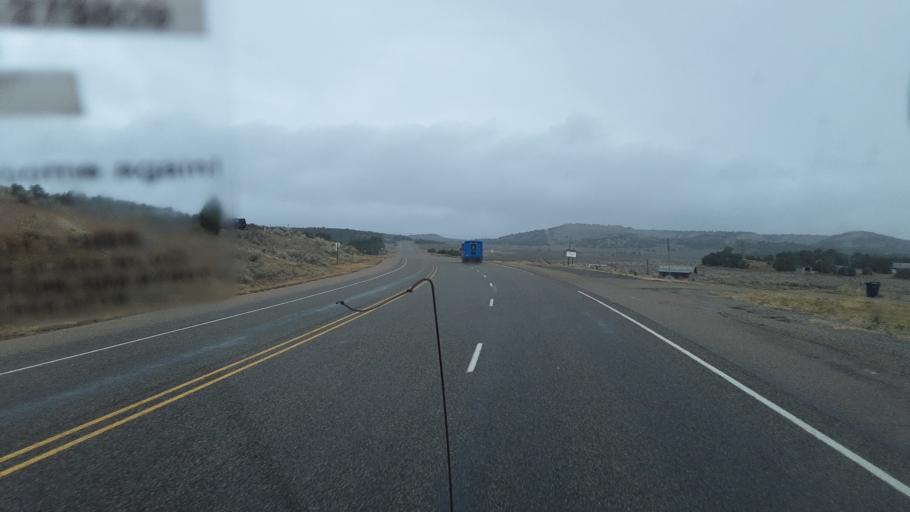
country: US
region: New Mexico
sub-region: Rio Arriba County
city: Tierra Amarilla
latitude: 36.4380
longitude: -106.4736
